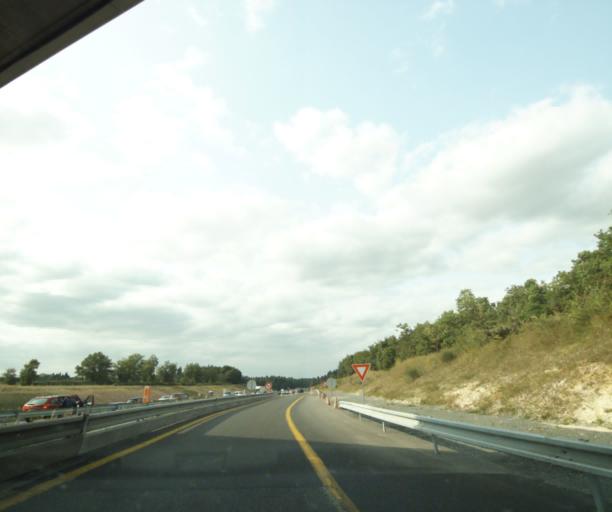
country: FR
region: Centre
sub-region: Departement d'Indre-et-Loire
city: Montbazon
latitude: 47.3050
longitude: 0.6926
